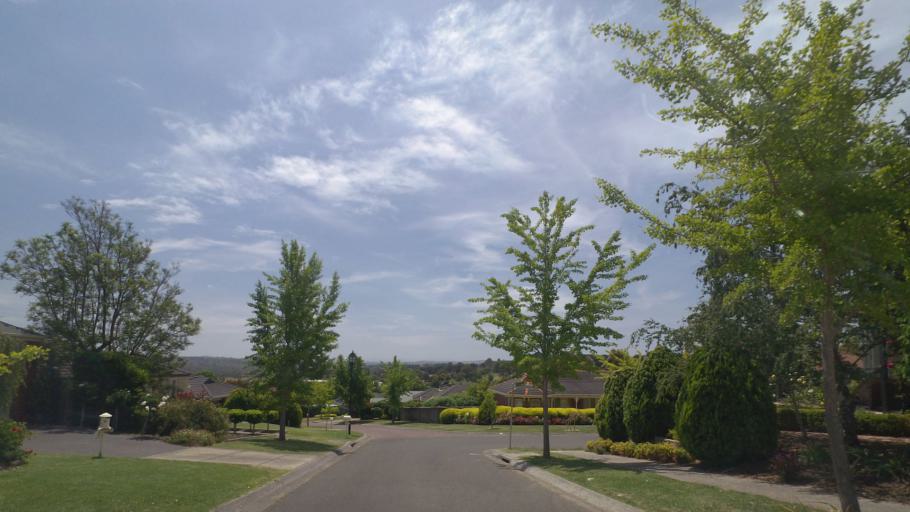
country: AU
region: Victoria
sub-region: Maroondah
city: Croydon North
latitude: -37.7602
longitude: 145.3032
